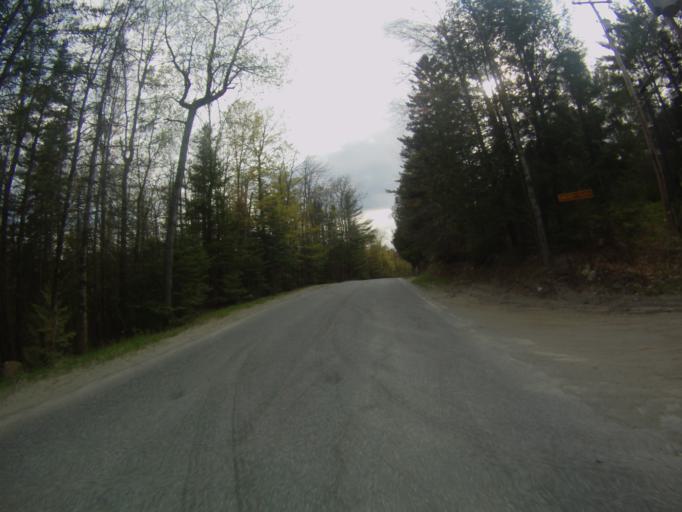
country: US
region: New York
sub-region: Warren County
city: Warrensburg
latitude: 43.8406
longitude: -73.8385
